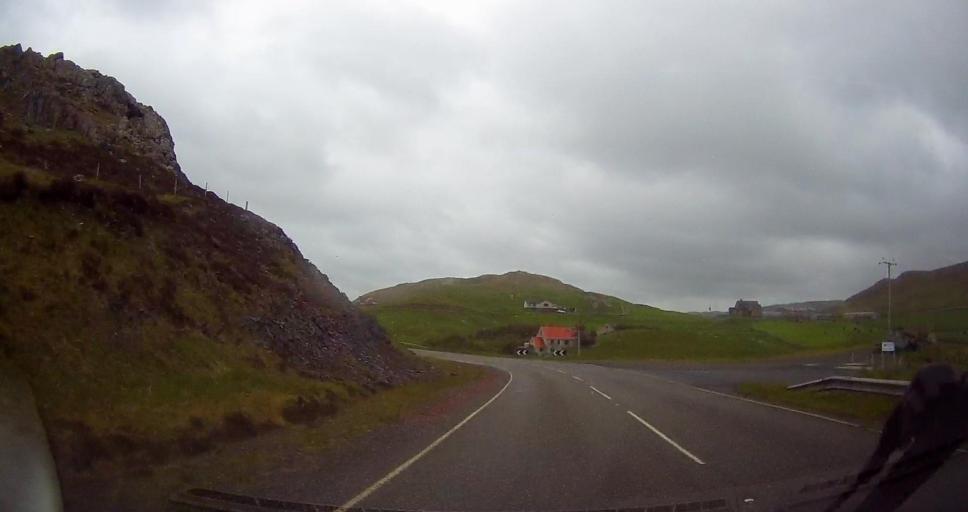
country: GB
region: Scotland
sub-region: Shetland Islands
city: Lerwick
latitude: 60.4086
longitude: -1.3893
